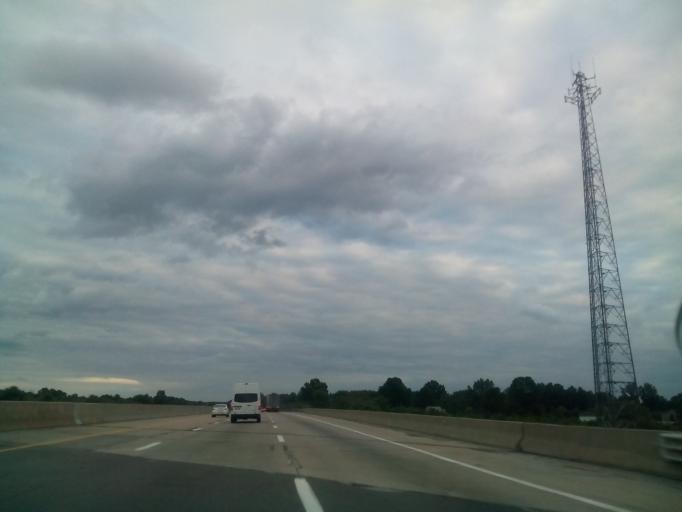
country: US
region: Ohio
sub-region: Trumbull County
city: Newton Falls
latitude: 41.1871
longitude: -80.9350
